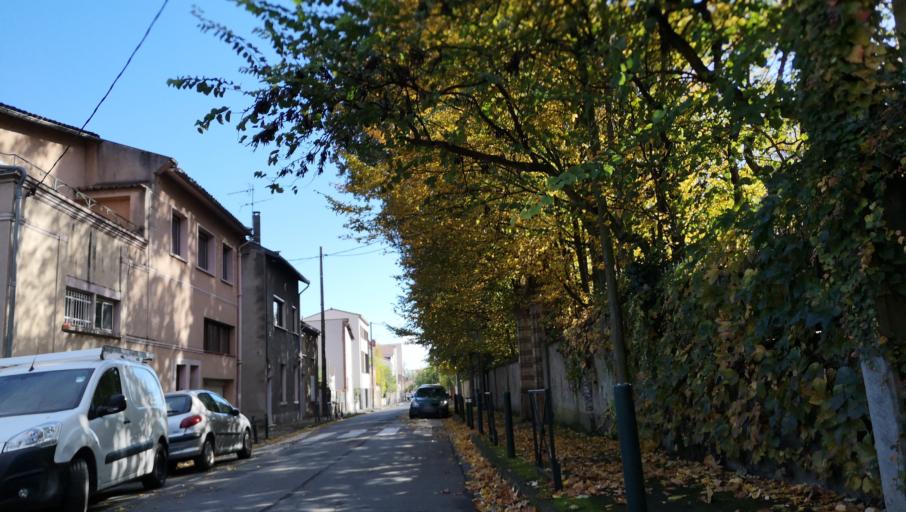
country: FR
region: Midi-Pyrenees
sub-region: Departement de la Haute-Garonne
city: Toulouse
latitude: 43.6082
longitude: 1.4169
